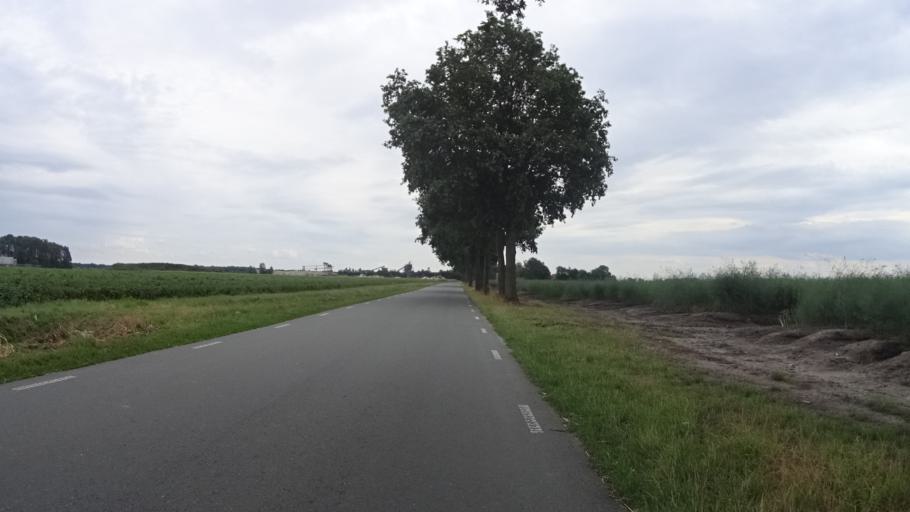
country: NL
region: Groningen
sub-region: Gemeente Slochteren
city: Slochteren
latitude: 53.1912
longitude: 6.8507
